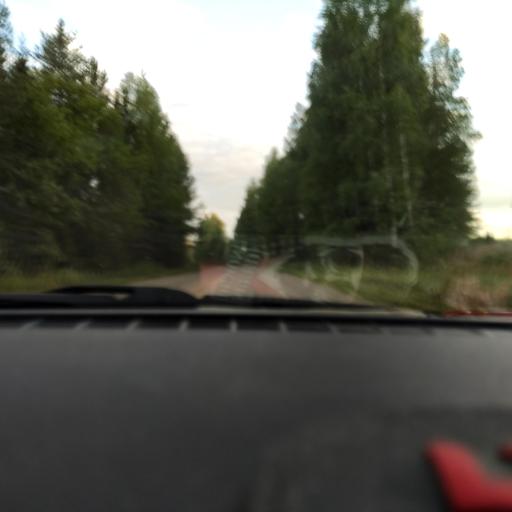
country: RU
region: Perm
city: Ocher
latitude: 57.9621
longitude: 54.8174
